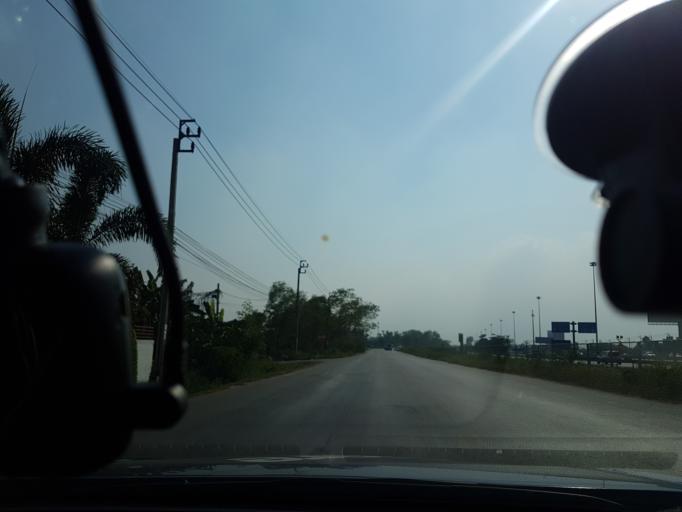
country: TH
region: Pathum Thani
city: Lam Luk Ka
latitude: 13.9122
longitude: 100.7014
